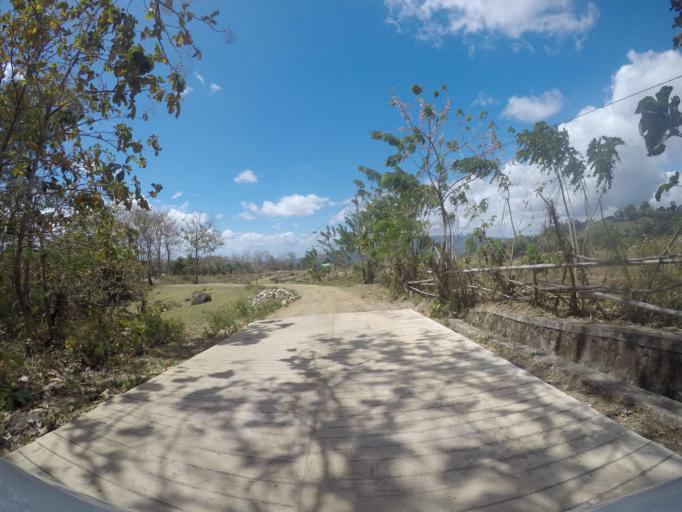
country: TL
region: Lautem
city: Lospalos
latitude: -8.5316
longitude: 126.7994
